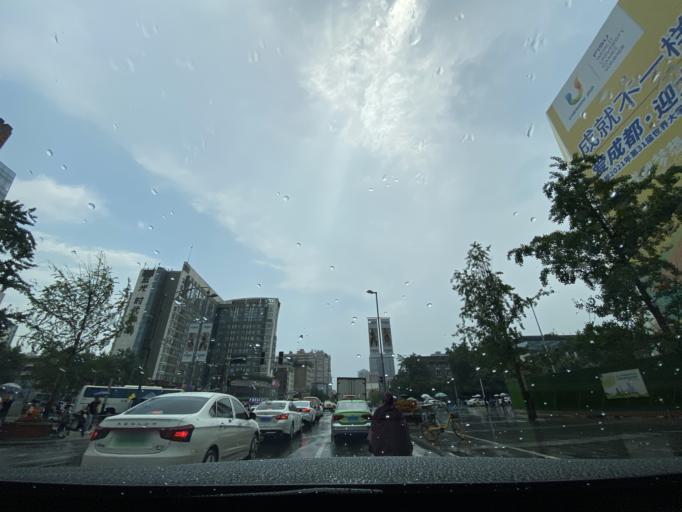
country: CN
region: Sichuan
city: Chengdu
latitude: 30.6555
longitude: 104.0762
